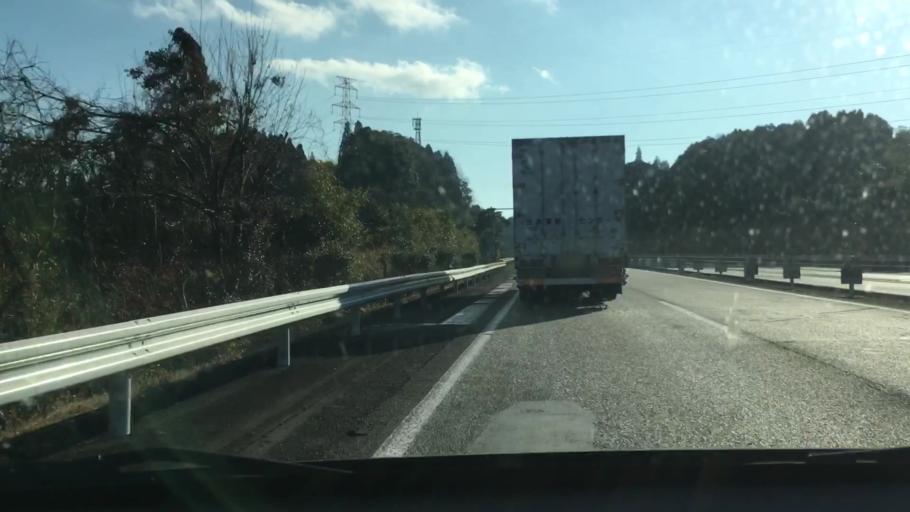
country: JP
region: Kagoshima
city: Okuchi-shinohara
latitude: 31.9313
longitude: 130.7059
